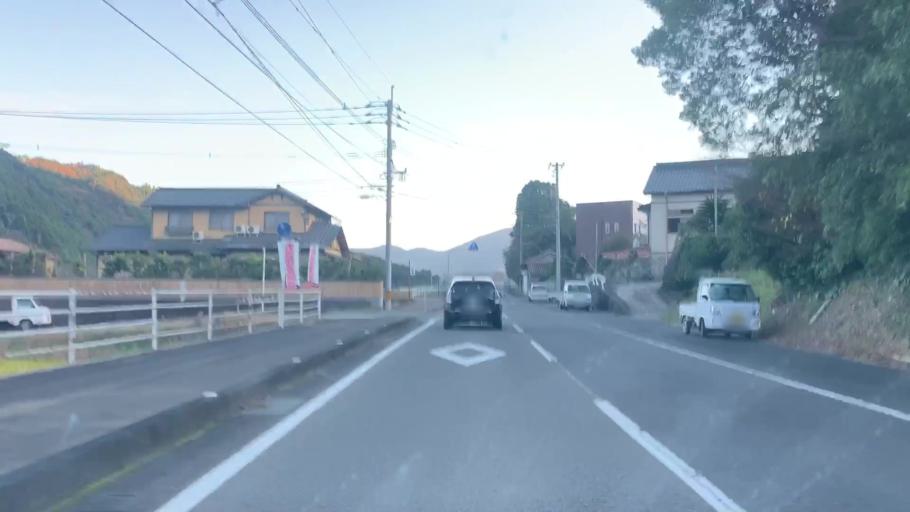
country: JP
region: Saga Prefecture
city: Imaricho-ko
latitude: 33.3256
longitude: 129.9687
